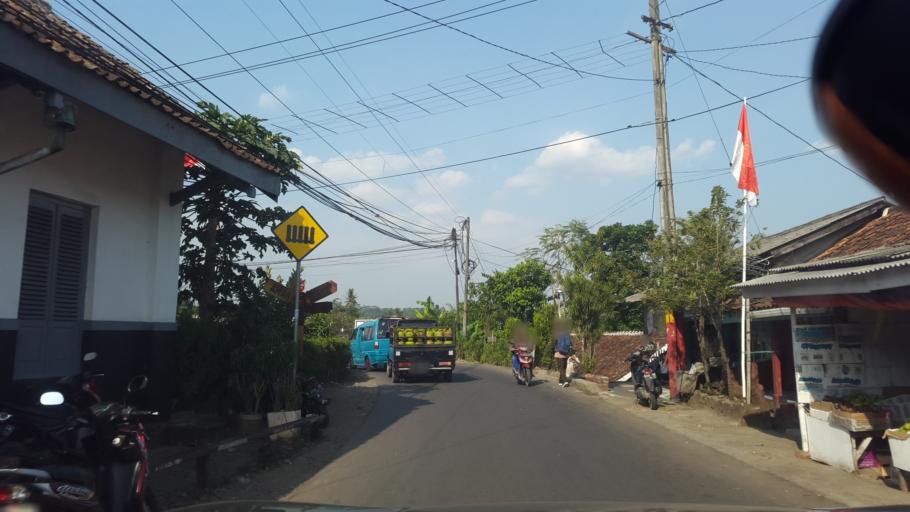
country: ID
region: West Java
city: Gunungkalong
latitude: -6.8965
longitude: 106.8224
